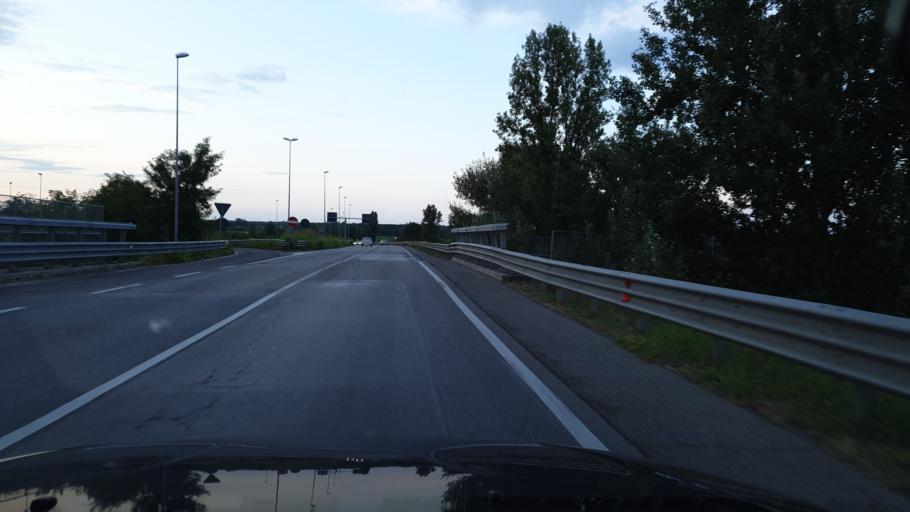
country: IT
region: Emilia-Romagna
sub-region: Provincia di Ravenna
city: Savio
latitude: 44.3162
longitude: 12.2843
